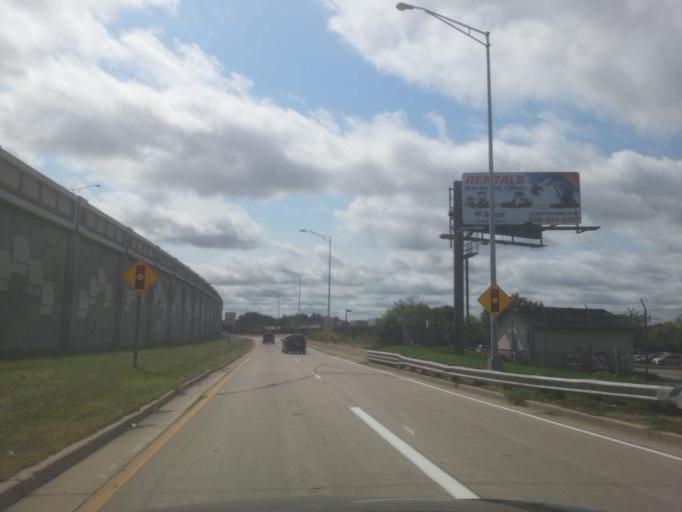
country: US
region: Wisconsin
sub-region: Dane County
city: Monona
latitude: 43.1017
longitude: -89.3170
